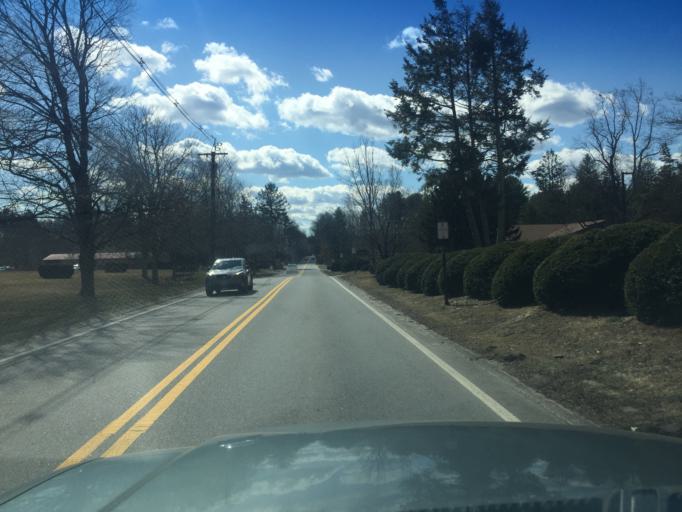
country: US
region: Massachusetts
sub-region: Middlesex County
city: Holliston
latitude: 42.1800
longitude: -71.4443
